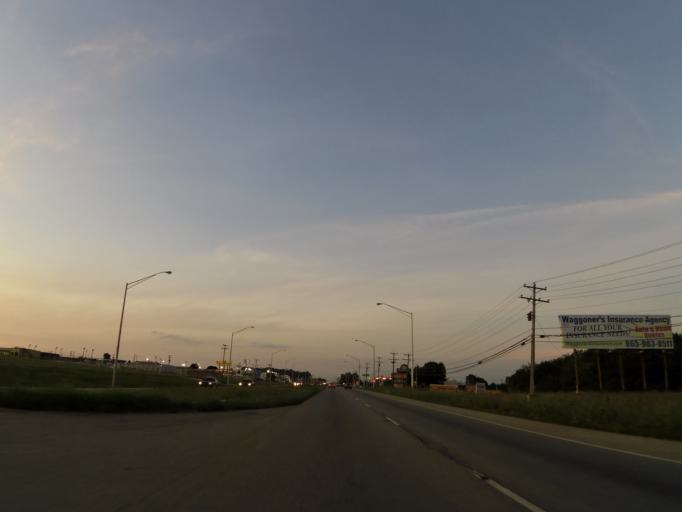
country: US
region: Tennessee
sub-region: Blount County
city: Alcoa
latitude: 35.8224
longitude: -83.9780
